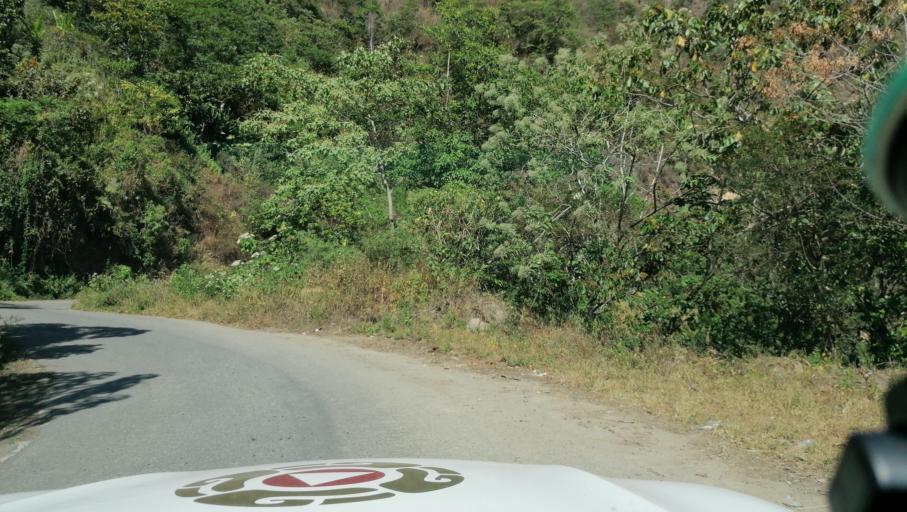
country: MX
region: Chiapas
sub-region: Cacahoatan
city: Benito Juarez
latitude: 15.1821
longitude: -92.1910
